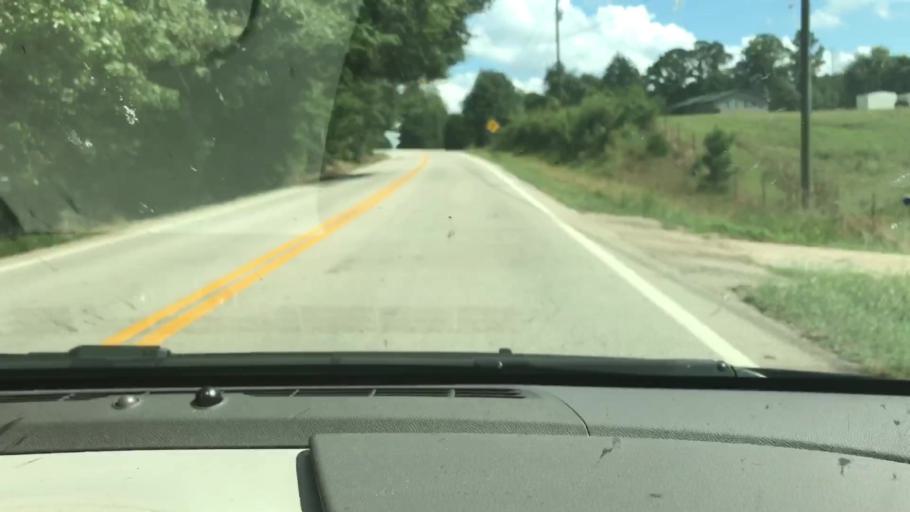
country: US
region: Georgia
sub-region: Troup County
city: La Grange
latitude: 32.8963
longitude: -85.0314
